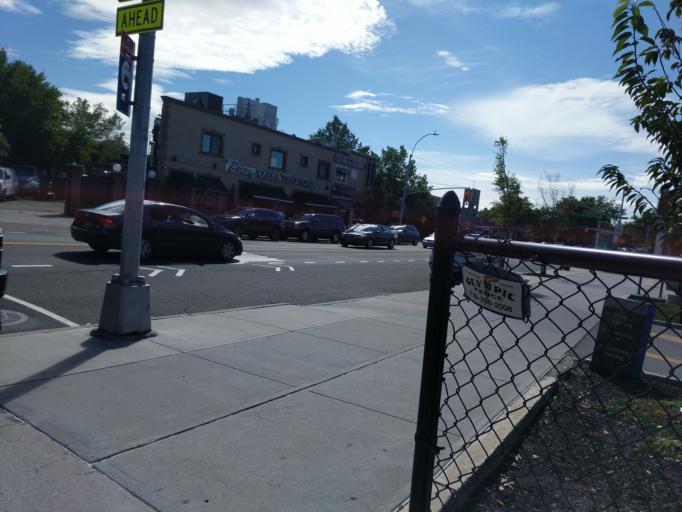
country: US
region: New York
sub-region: Kings County
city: East New York
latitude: 40.7224
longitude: -73.8852
